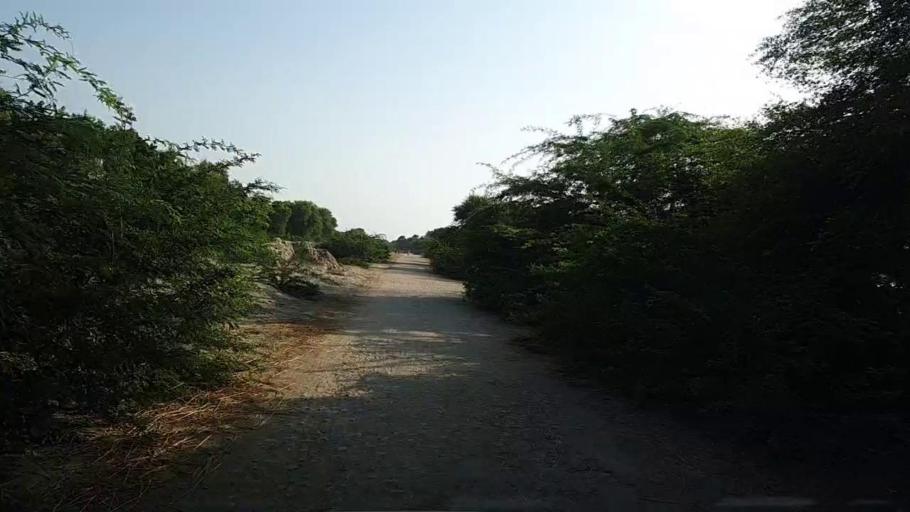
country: PK
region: Sindh
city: Kario
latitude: 24.7867
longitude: 68.6700
